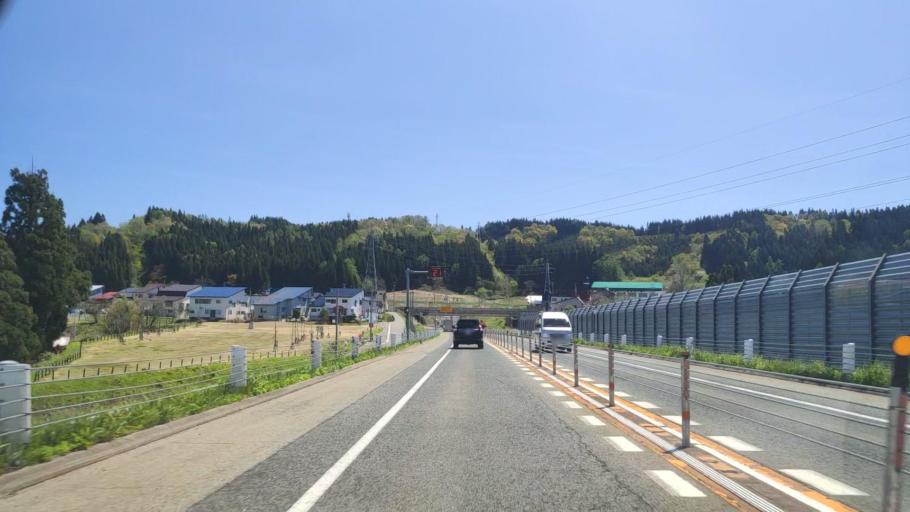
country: JP
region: Yamagata
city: Shinjo
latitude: 38.6926
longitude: 140.3120
